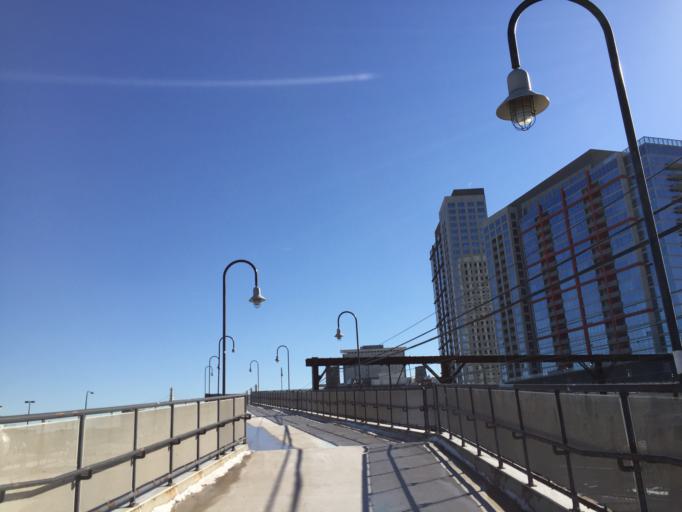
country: US
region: Illinois
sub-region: Cook County
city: Chicago
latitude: 41.8587
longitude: -87.6180
